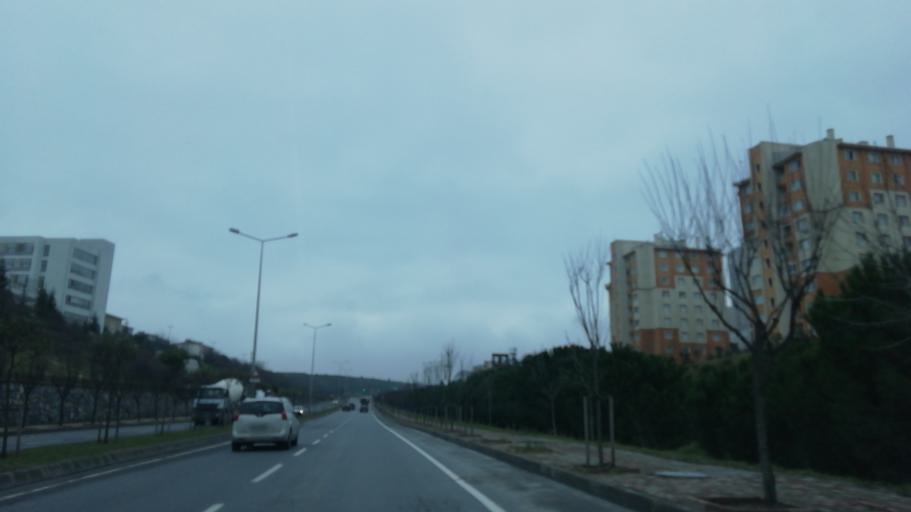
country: TR
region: Istanbul
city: Basaksehir
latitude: 41.1015
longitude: 28.8008
